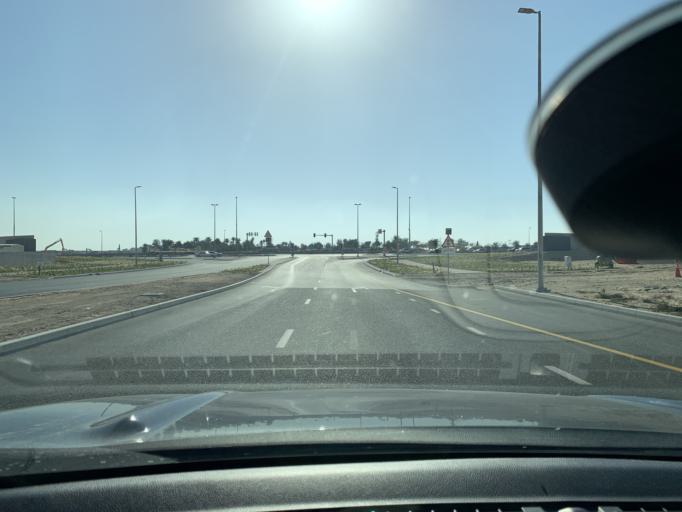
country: AE
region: Dubai
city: Dubai
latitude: 25.0320
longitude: 55.2356
